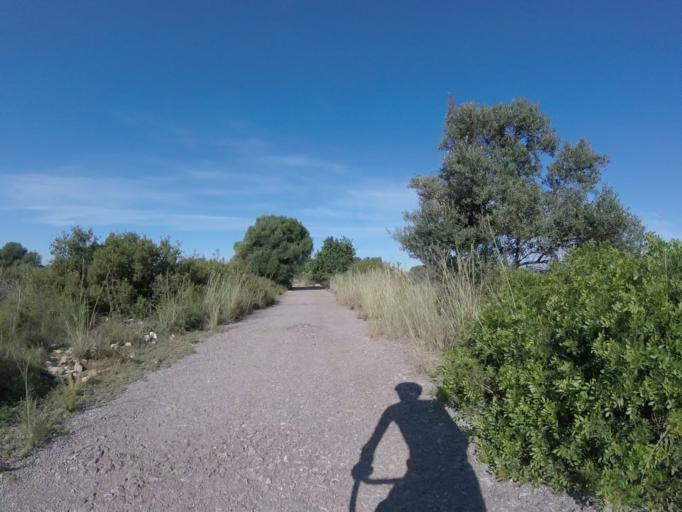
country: ES
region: Valencia
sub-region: Provincia de Castello
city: Torreblanca
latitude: 40.2075
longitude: 0.2461
